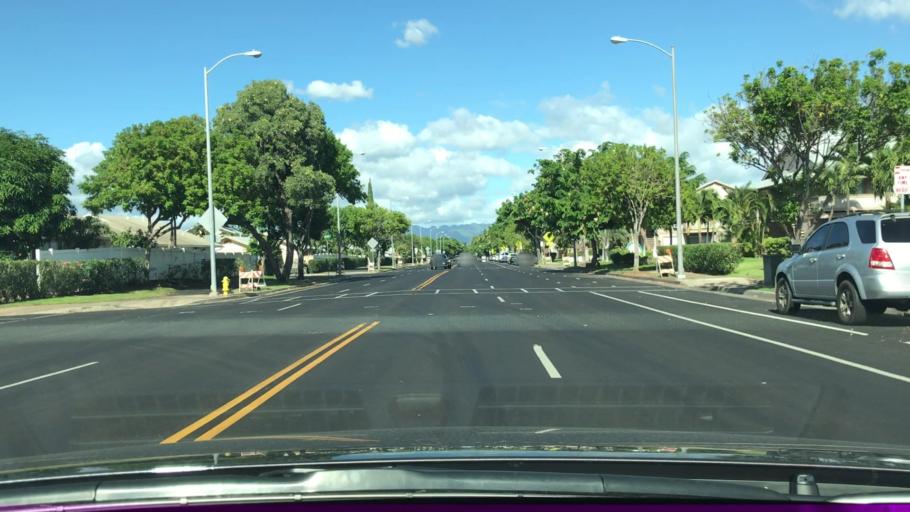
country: US
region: Hawaii
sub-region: Honolulu County
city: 'Ewa Gentry
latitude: 21.3390
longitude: -158.0312
